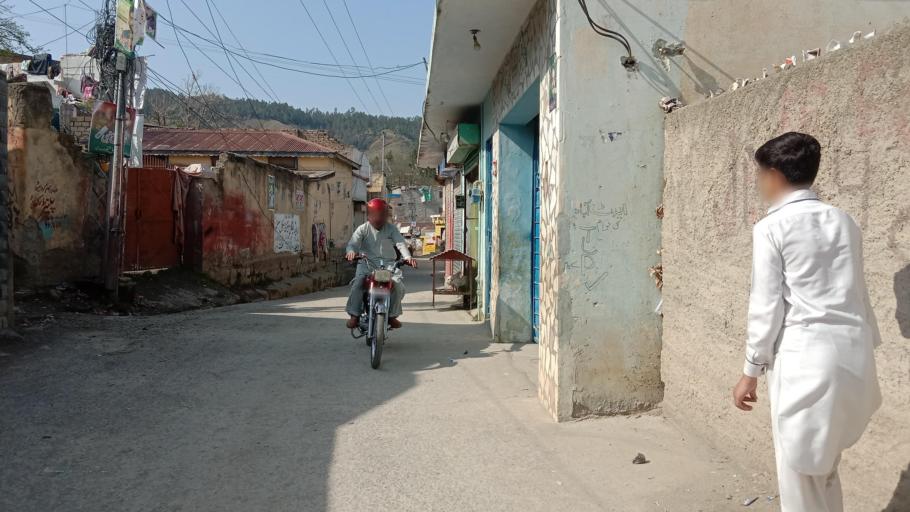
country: PK
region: Khyber Pakhtunkhwa
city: Abbottabad
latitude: 34.1751
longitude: 73.2169
